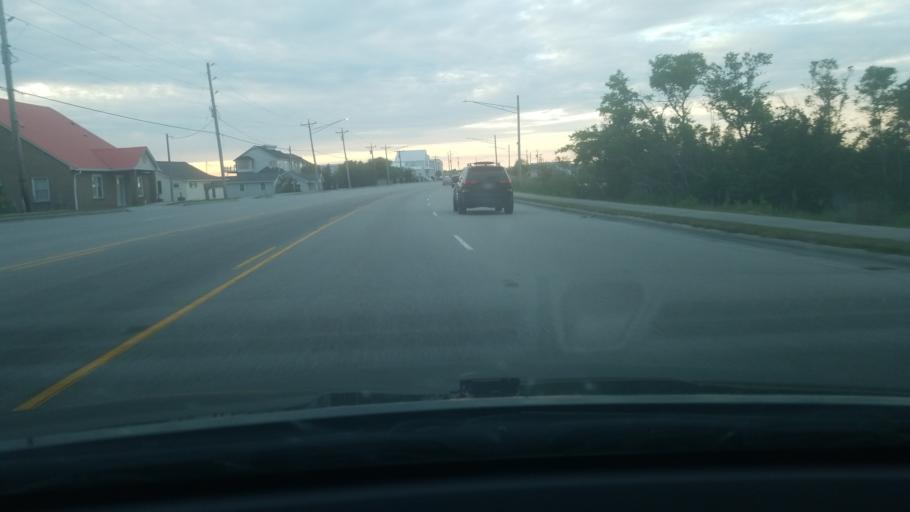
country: US
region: North Carolina
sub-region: Onslow County
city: Swansboro
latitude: 34.6785
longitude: -77.1086
